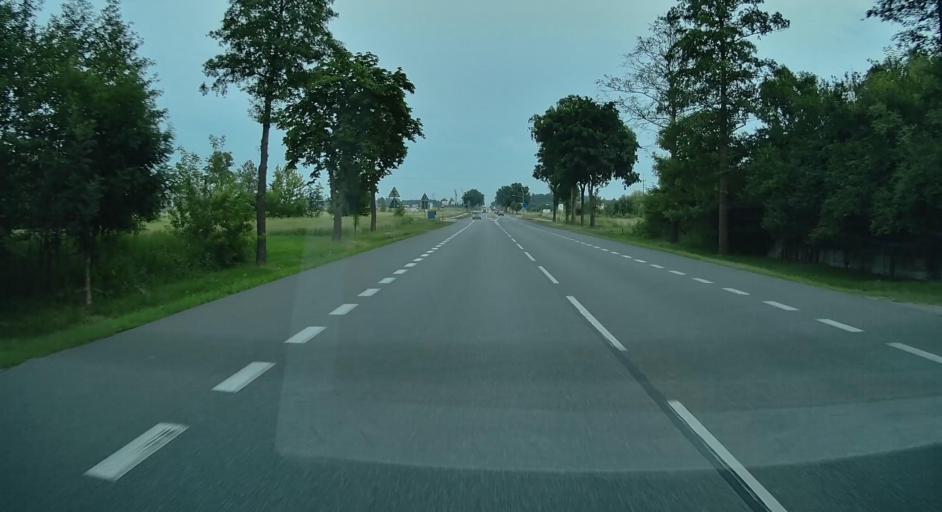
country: PL
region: Masovian Voivodeship
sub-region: Siedlce
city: Siedlce
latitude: 52.1293
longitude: 22.3361
